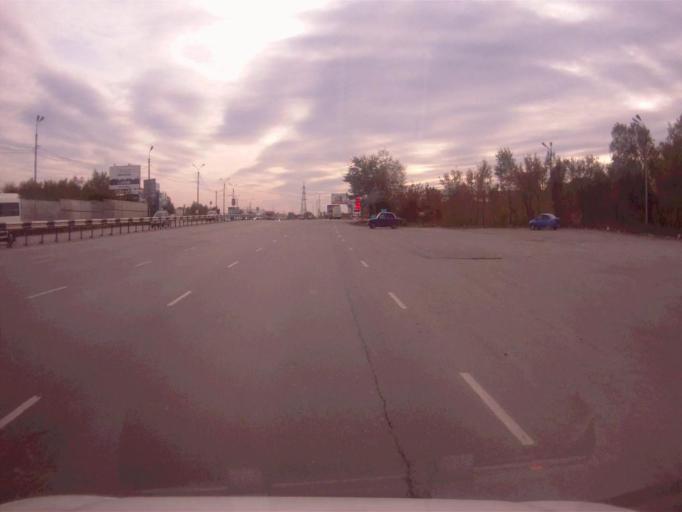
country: RU
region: Chelyabinsk
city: Novosineglazovskiy
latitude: 55.0771
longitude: 61.3881
